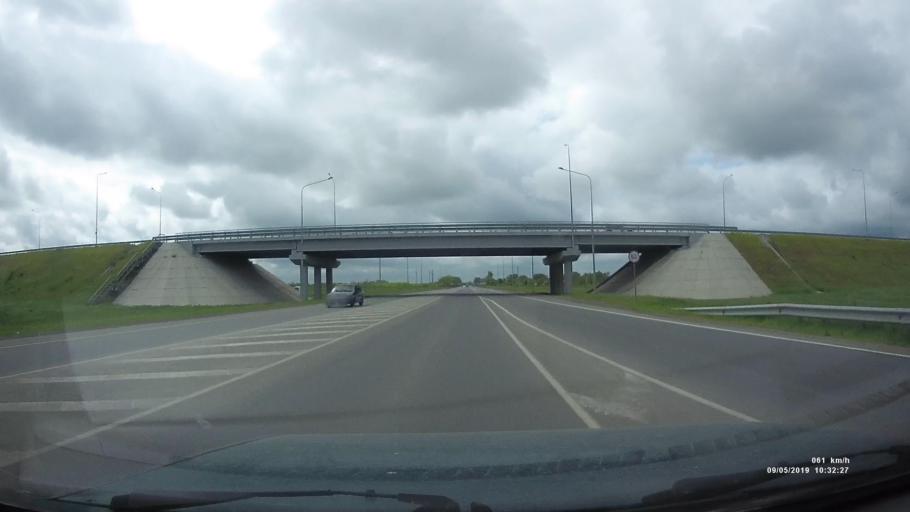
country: RU
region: Rostov
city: Azov
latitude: 47.0724
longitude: 39.4262
